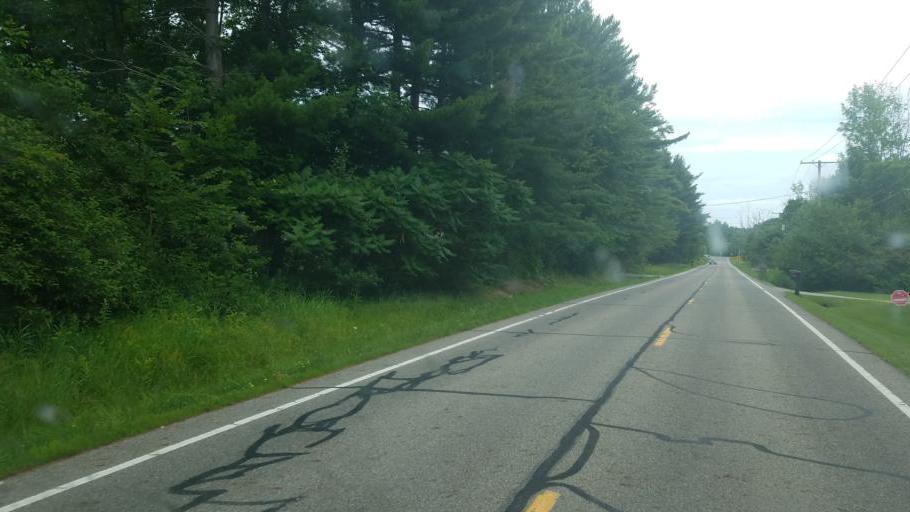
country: US
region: Ohio
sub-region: Geauga County
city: Burton
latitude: 41.4439
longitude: -81.2457
